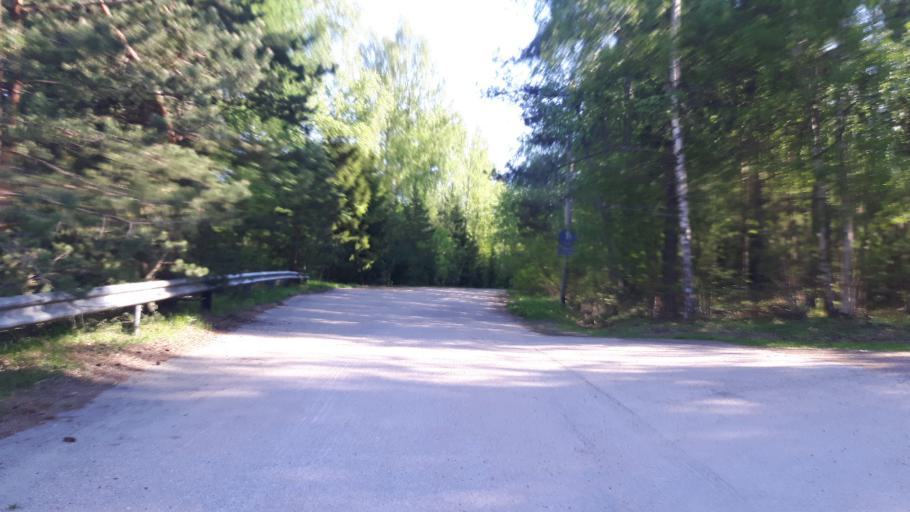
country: FI
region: Kymenlaakso
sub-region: Kotka-Hamina
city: Kotka
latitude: 60.4505
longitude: 26.8951
